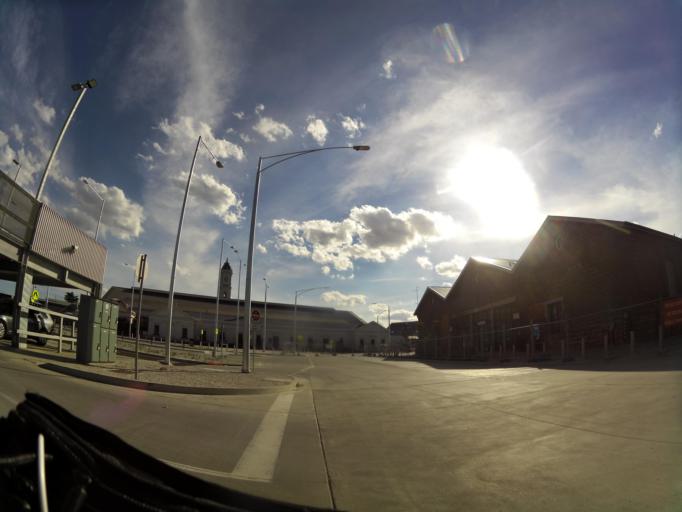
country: AU
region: Victoria
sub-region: Ballarat North
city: Soldiers Hill
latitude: -37.5579
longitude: 143.8602
